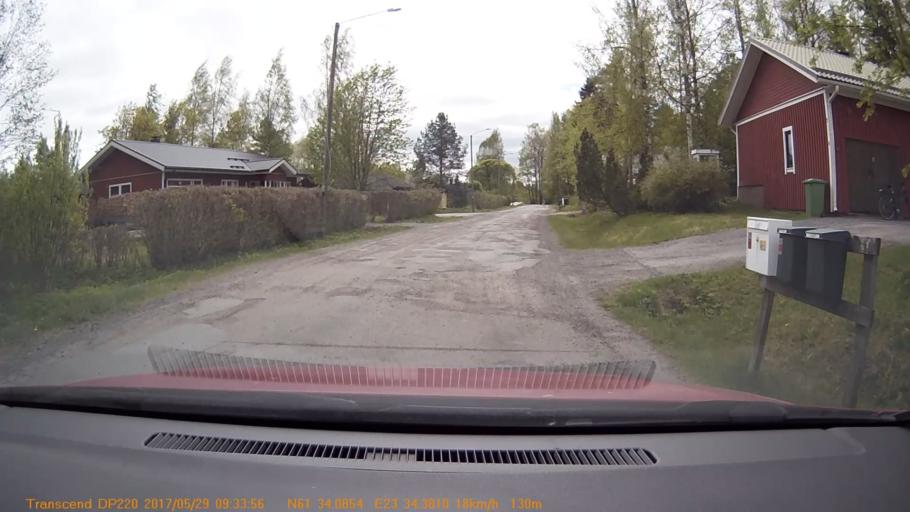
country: FI
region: Pirkanmaa
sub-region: Tampere
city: Yloejaervi
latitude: 61.5681
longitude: 23.5730
